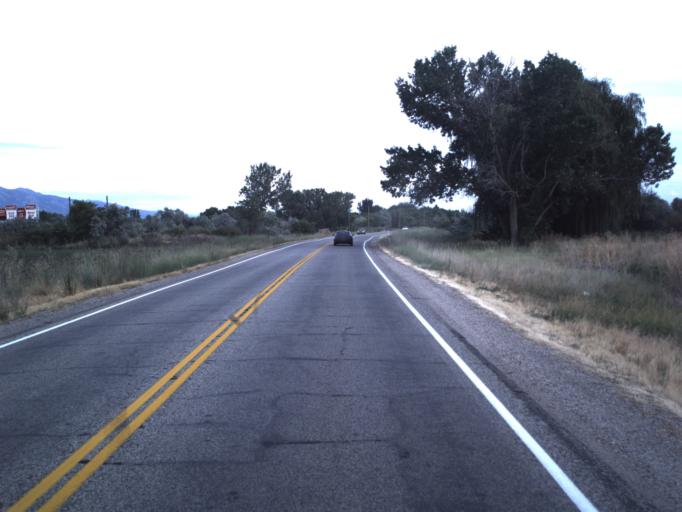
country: US
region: Utah
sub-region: Weber County
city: Marriott-Slaterville
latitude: 41.2608
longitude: -112.0257
